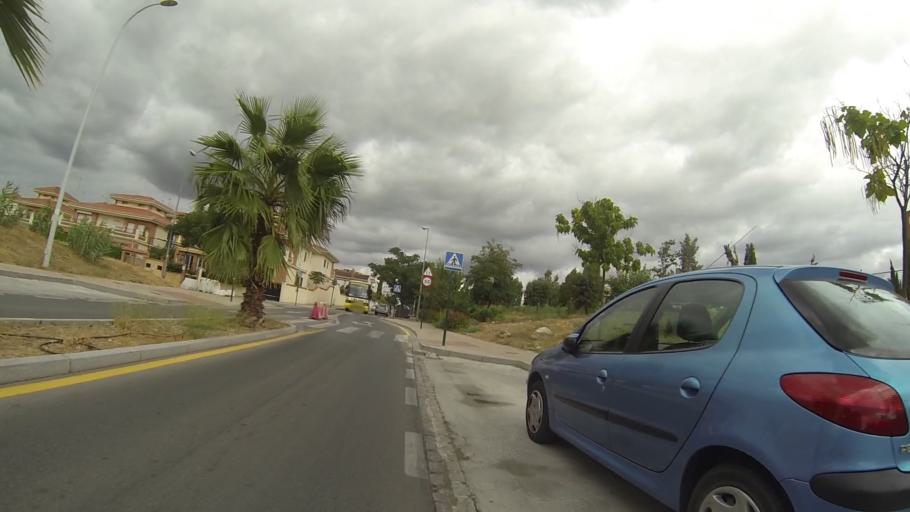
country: ES
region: Andalusia
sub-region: Provincia de Granada
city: Granada
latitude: 37.1929
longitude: -3.6201
